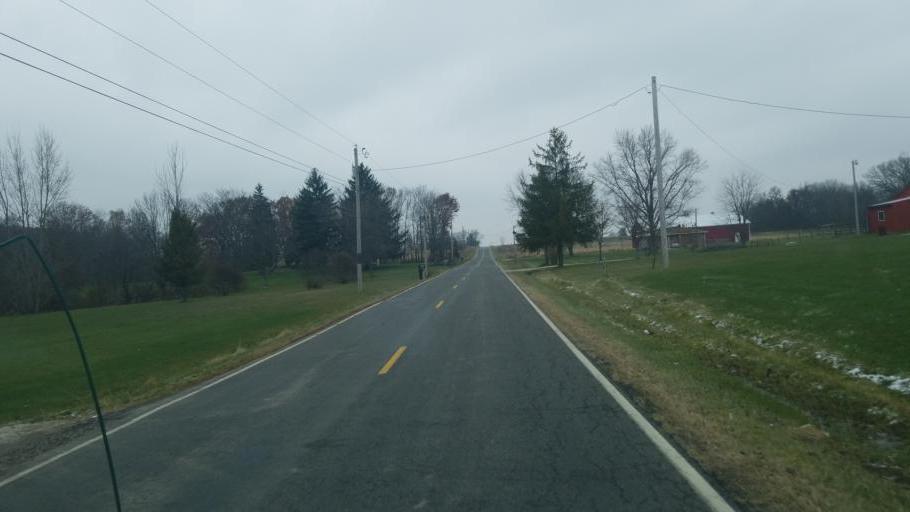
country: US
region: Ohio
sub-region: Medina County
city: Lodi
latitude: 41.1283
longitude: -82.0021
